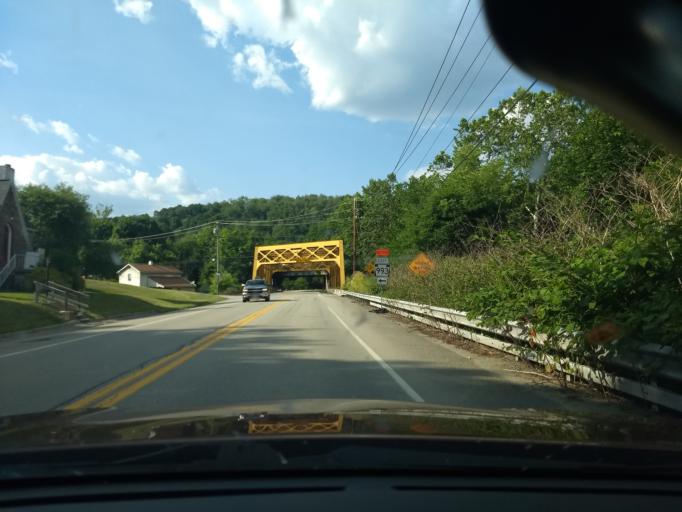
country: US
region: Pennsylvania
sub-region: Westmoreland County
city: Irwin
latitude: 40.3429
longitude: -79.7248
